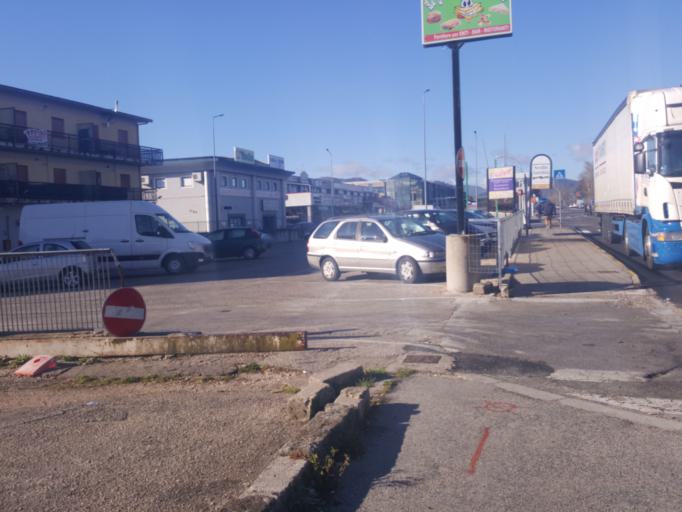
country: IT
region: Abruzzo
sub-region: Provincia dell' Aquila
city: Carsoli
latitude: 42.0848
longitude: 13.0627
